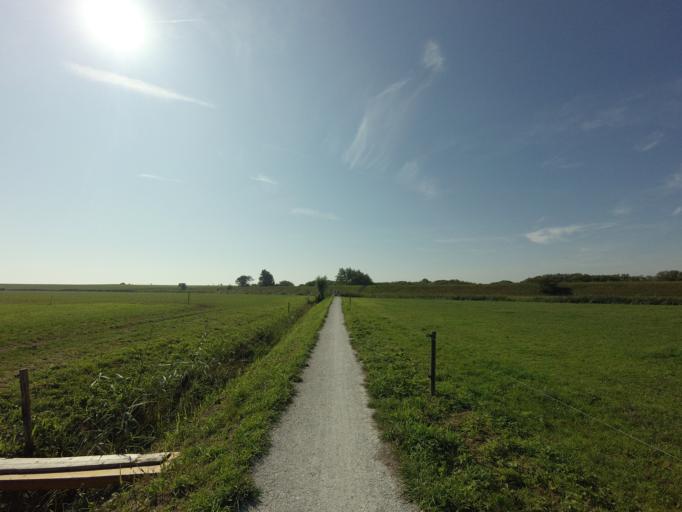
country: NL
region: Friesland
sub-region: Gemeente Schiermonnikoog
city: Schiermonnikoog
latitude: 53.4739
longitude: 6.1551
